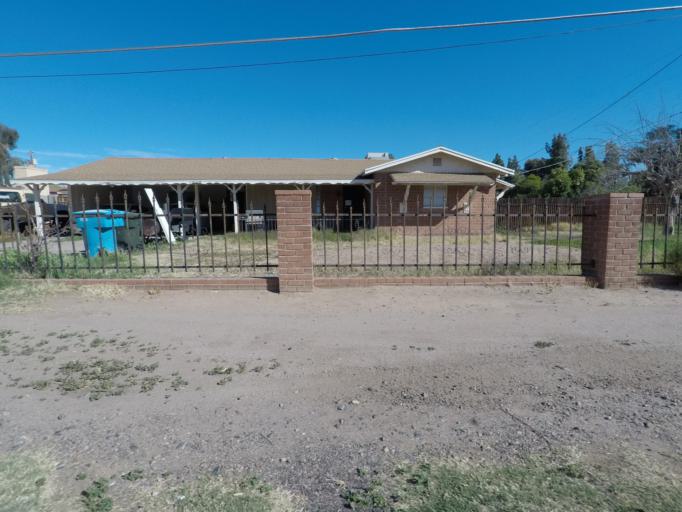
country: US
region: Arizona
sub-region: Maricopa County
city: Glendale
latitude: 33.5459
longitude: -112.1329
